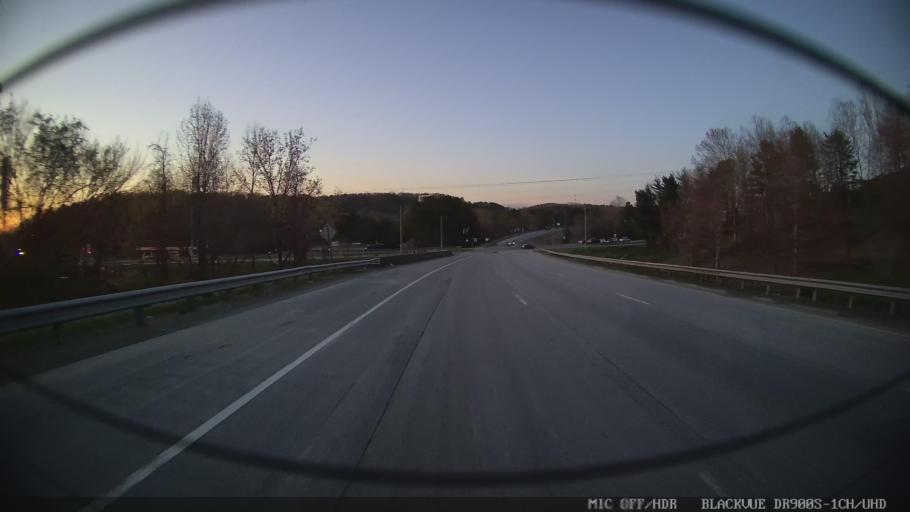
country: US
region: Georgia
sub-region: Bartow County
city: Cartersville
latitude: 34.2054
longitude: -84.7584
